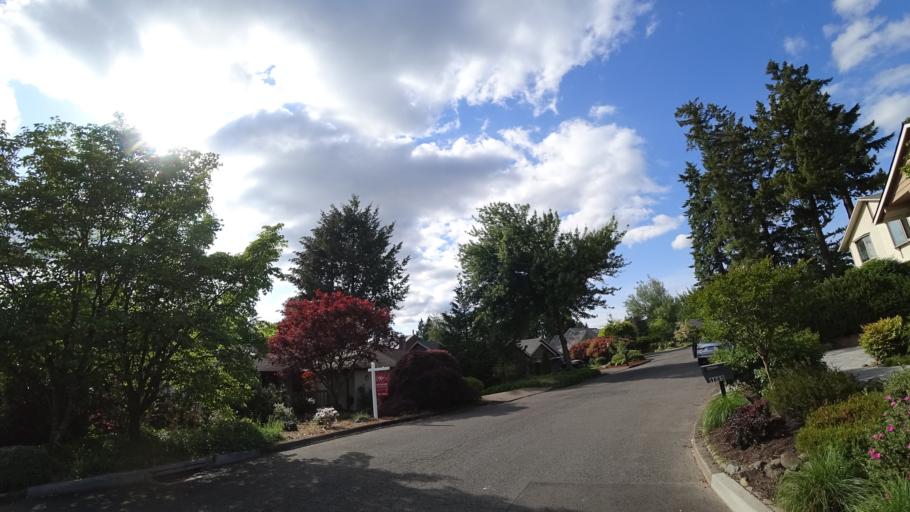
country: US
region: Oregon
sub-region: Washington County
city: Raleigh Hills
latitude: 45.4821
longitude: -122.7252
